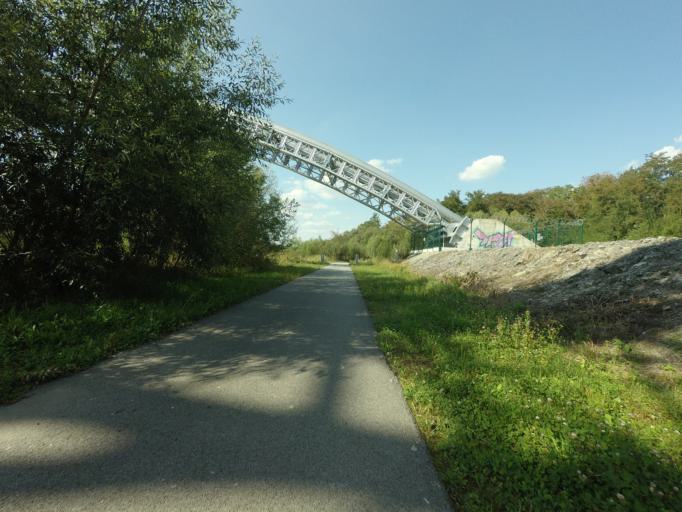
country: CZ
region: Jihocesky
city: Tyn nad Vltavou
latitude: 49.1966
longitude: 14.4456
